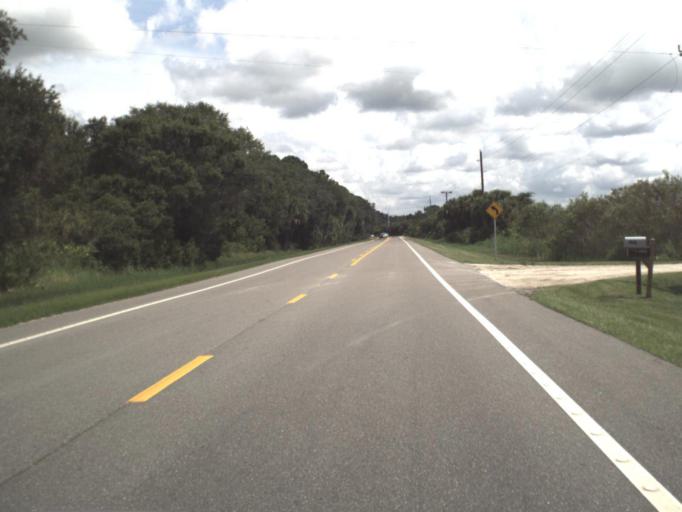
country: US
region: Florida
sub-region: Sarasota County
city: Lake Sarasota
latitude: 27.2531
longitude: -82.3932
